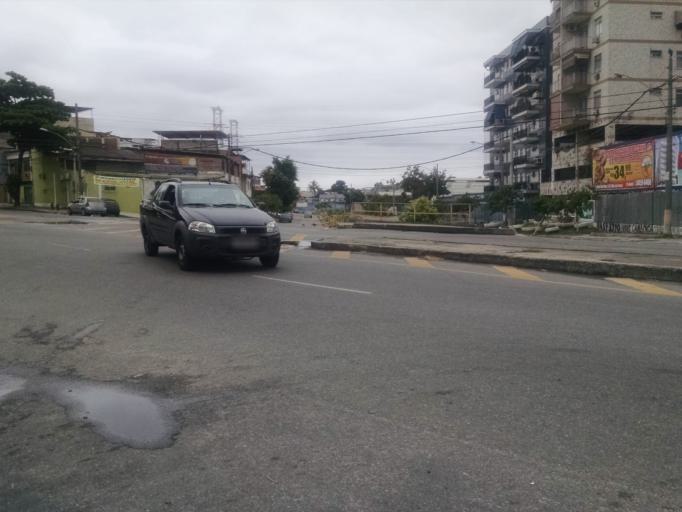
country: BR
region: Rio de Janeiro
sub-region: Duque De Caxias
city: Duque de Caxias
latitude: -22.8336
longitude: -43.3092
